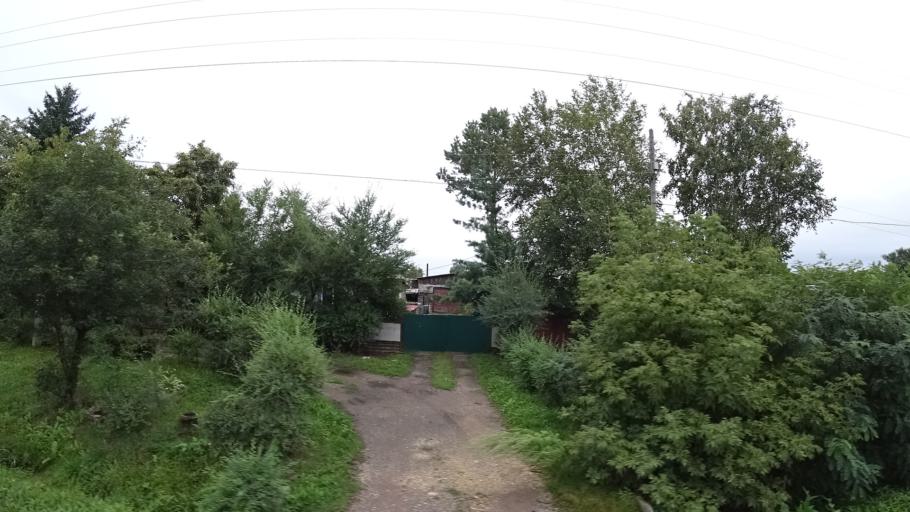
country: RU
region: Primorskiy
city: Chernigovka
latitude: 44.3385
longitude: 132.5913
